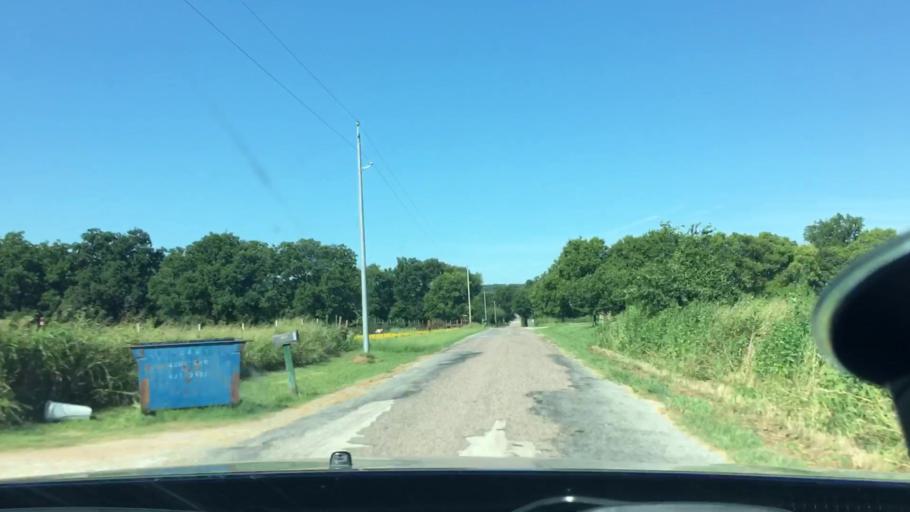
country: US
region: Oklahoma
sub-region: Pontotoc County
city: Ada
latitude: 34.7236
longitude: -96.6553
